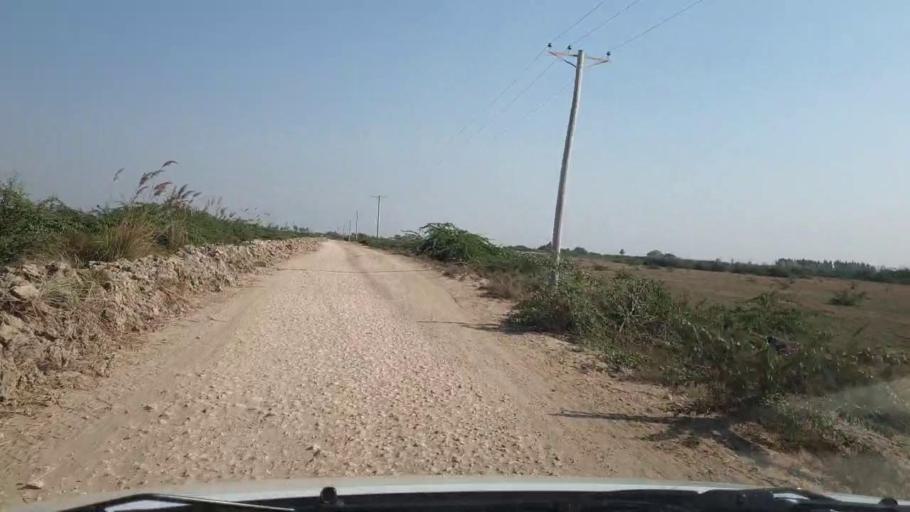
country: PK
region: Sindh
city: Gharo
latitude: 24.6495
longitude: 67.6257
